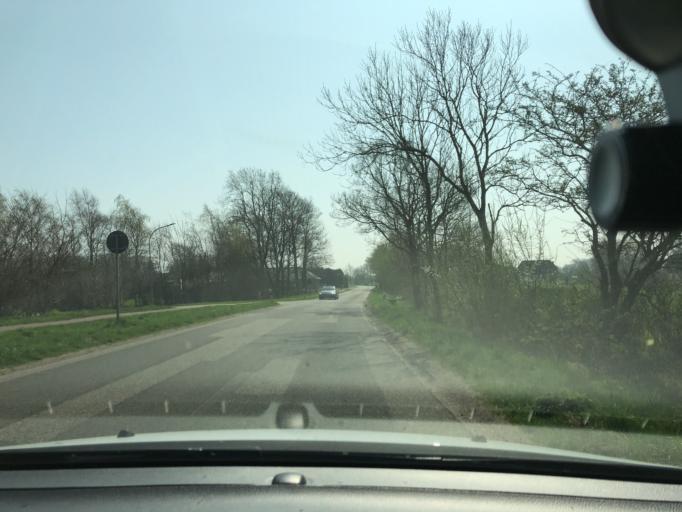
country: DE
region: Schleswig-Holstein
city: Grossenwiehe
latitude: 54.6902
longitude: 9.2403
